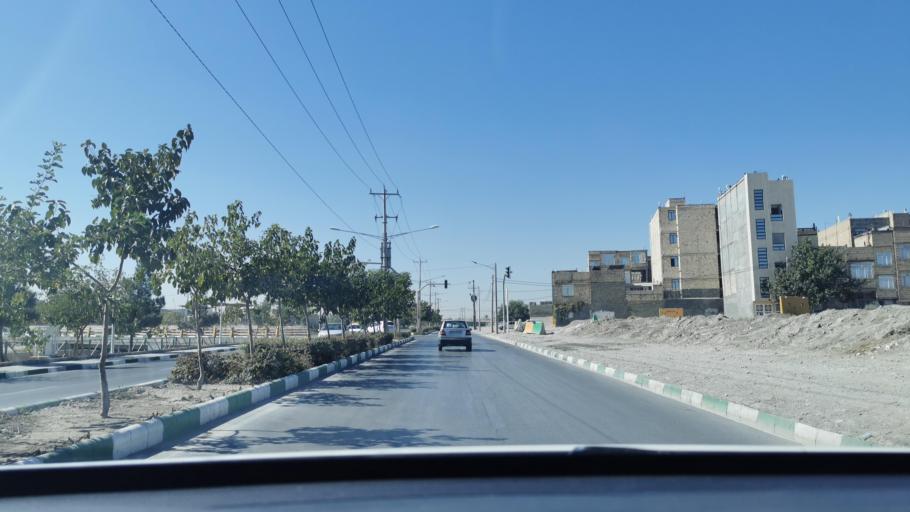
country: IR
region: Razavi Khorasan
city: Mashhad
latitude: 36.3363
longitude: 59.6112
